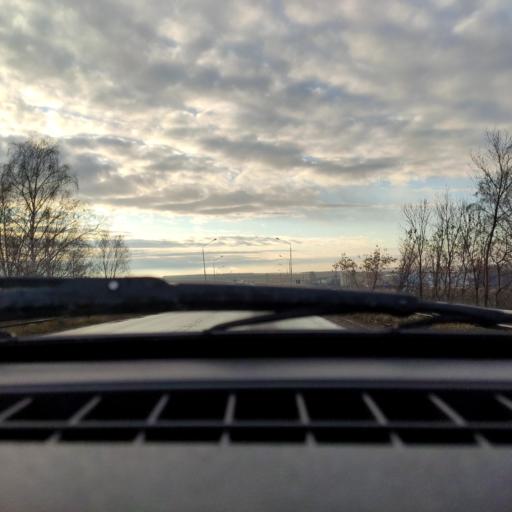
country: RU
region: Bashkortostan
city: Iglino
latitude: 54.7743
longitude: 56.2565
